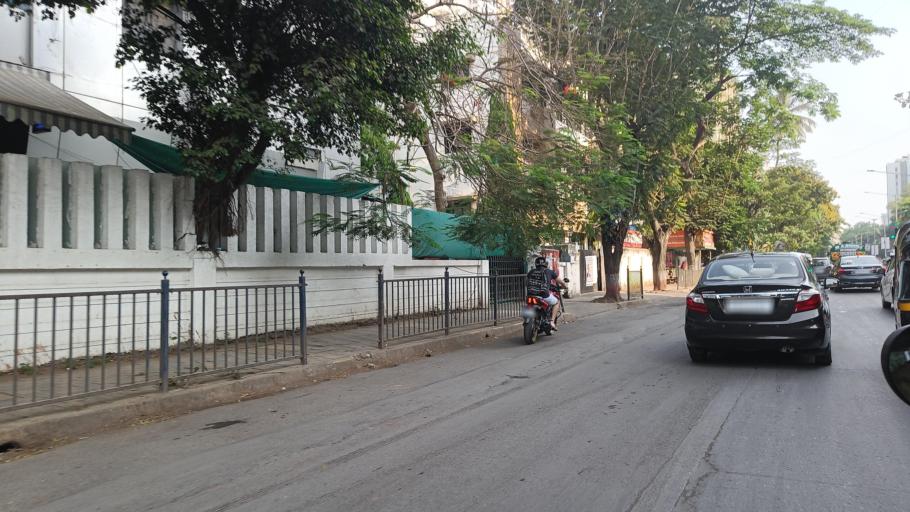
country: IN
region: Maharashtra
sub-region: Mumbai Suburban
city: Powai
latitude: 19.1336
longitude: 72.8257
